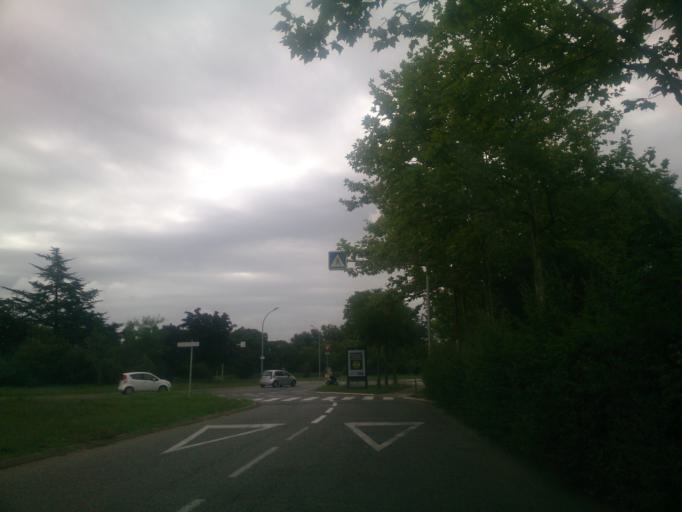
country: FR
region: Midi-Pyrenees
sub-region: Departement de la Haute-Garonne
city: Toulouse
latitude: 43.5741
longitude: 1.4040
